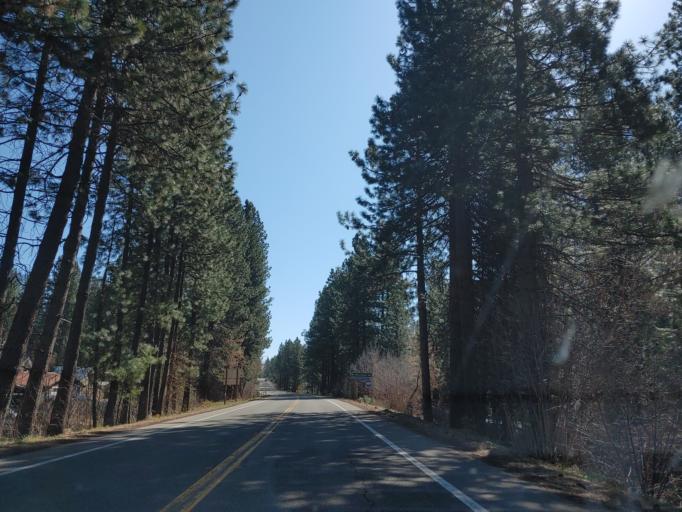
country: US
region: California
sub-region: Siskiyou County
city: McCloud
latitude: 41.2510
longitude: -122.1317
